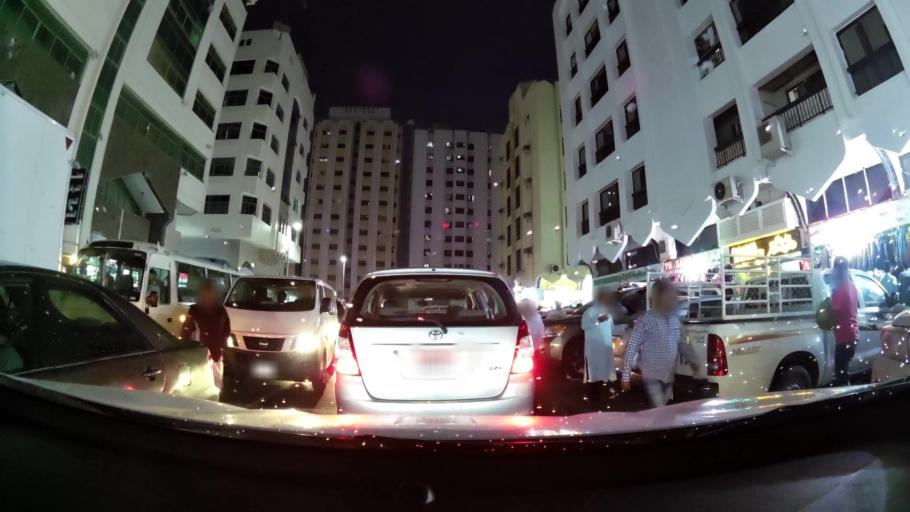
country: AE
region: Abu Dhabi
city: Abu Dhabi
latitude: 24.4863
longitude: 54.3612
